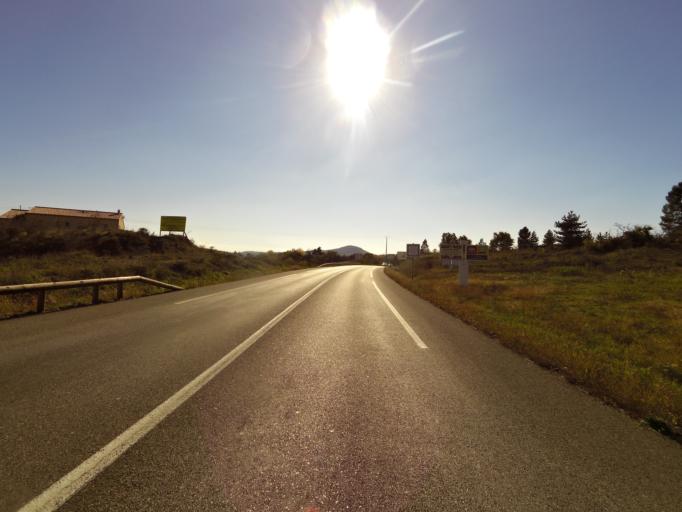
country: FR
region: Rhone-Alpes
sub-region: Departement de l'Ardeche
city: Saint-Etienne-de-Fontbellon
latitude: 44.5969
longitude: 4.3943
